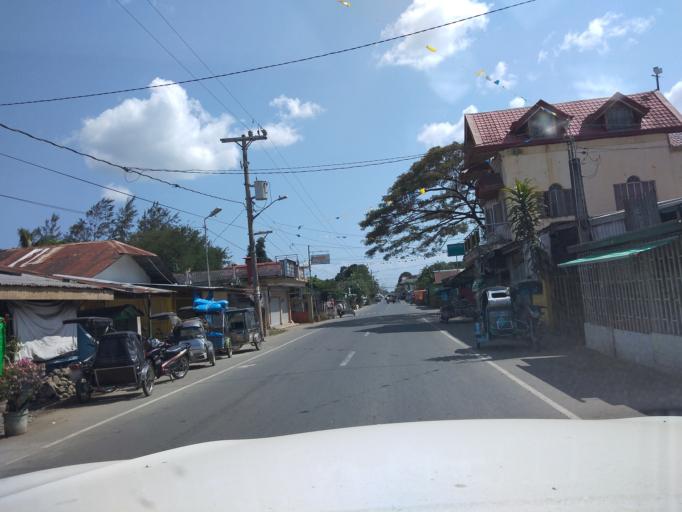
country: PH
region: Central Luzon
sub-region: Province of Pampanga
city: Bahay Pare
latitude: 15.0341
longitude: 120.8810
